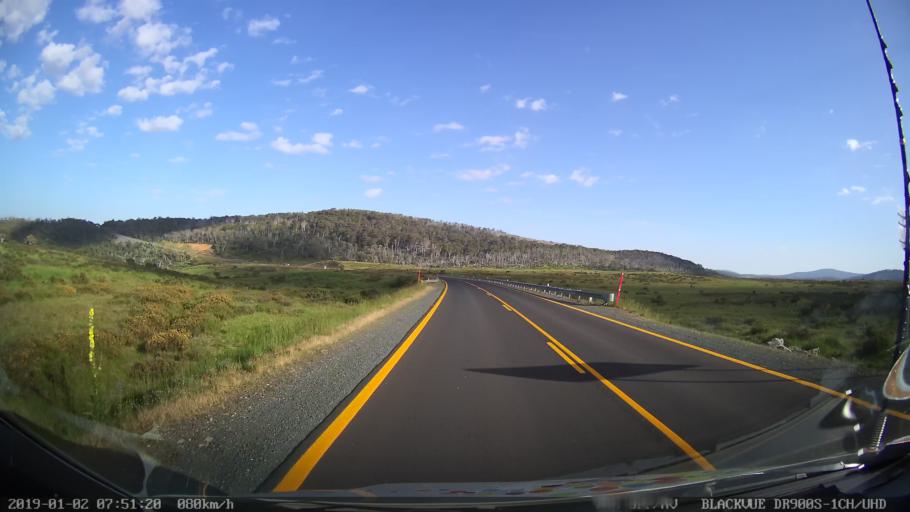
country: AU
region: New South Wales
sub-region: Tumut Shire
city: Tumut
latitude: -35.7194
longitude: 148.5311
